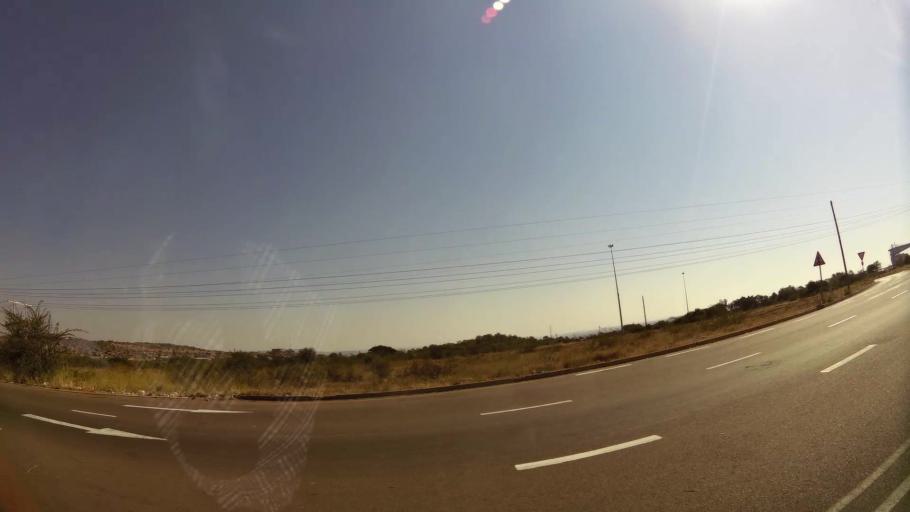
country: ZA
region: Gauteng
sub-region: City of Tshwane Metropolitan Municipality
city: Mabopane
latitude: -25.5245
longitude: 28.0873
